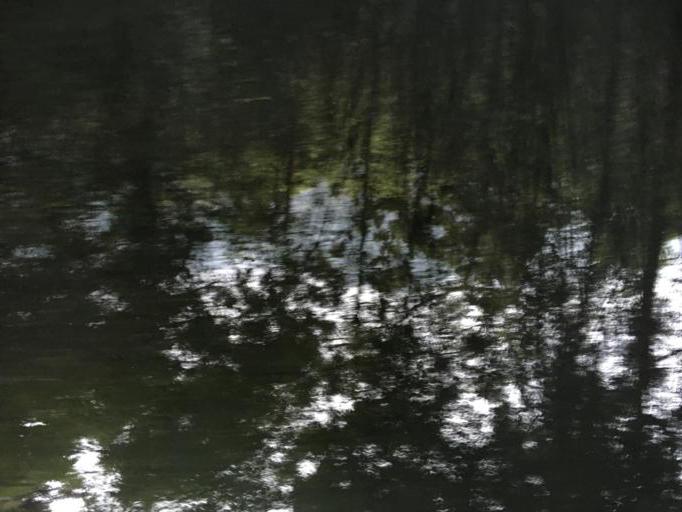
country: TW
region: Taiwan
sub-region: Chiayi
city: Jiayi Shi
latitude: 23.5278
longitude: 120.6542
